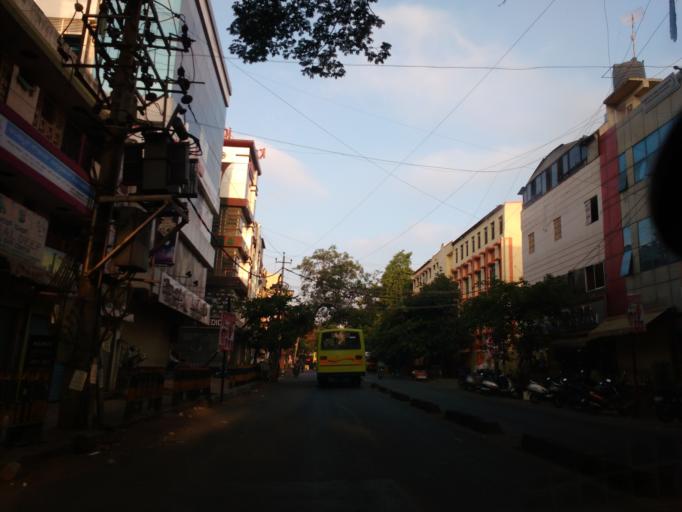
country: IN
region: Karnataka
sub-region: Bangalore Urban
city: Bangalore
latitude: 13.0040
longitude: 77.5510
